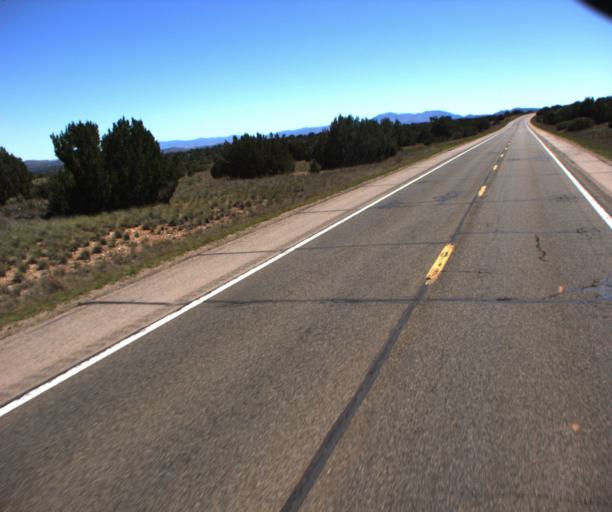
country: US
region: Arizona
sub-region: Yavapai County
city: Paulden
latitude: 34.9453
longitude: -112.4260
